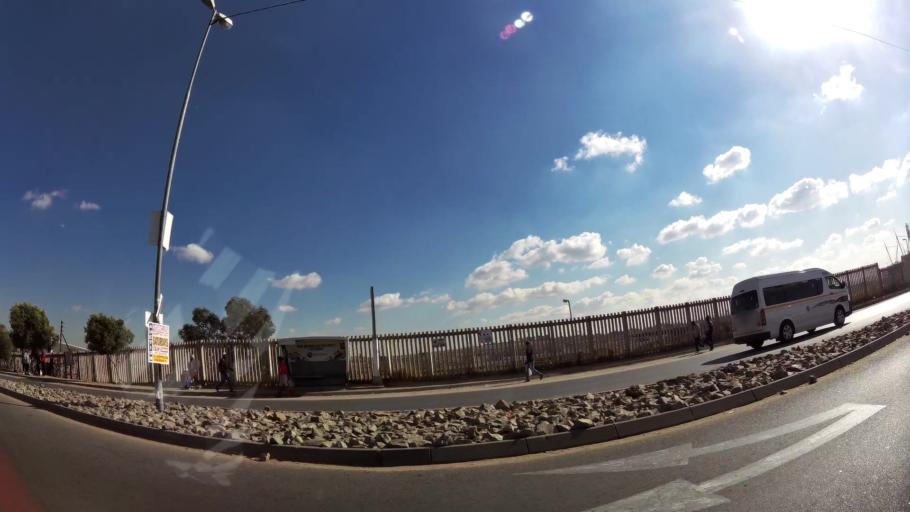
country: ZA
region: Gauteng
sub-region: West Rand District Municipality
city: Muldersdriseloop
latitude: -26.0173
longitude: 27.9384
